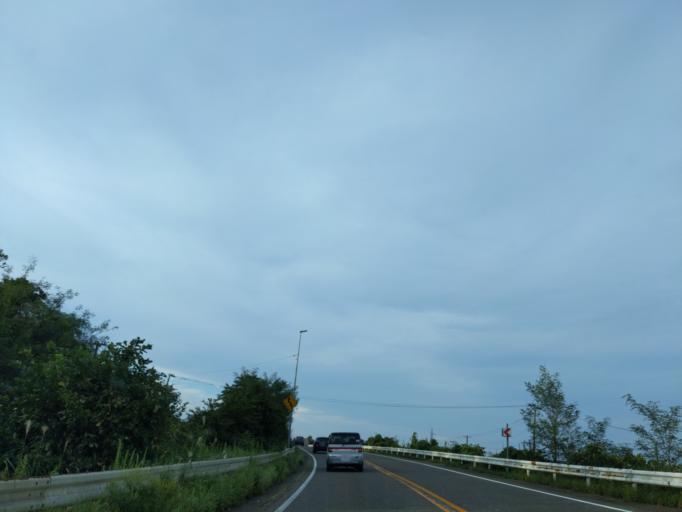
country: JP
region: Niigata
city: Joetsu
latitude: 37.2055
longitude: 138.3000
